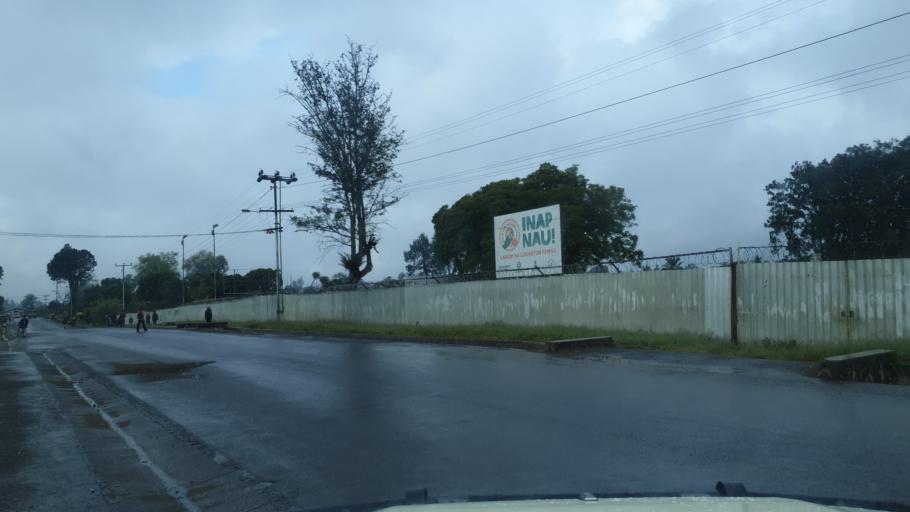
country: PG
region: Eastern Highlands
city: Goroka
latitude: -6.0849
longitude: 145.3880
